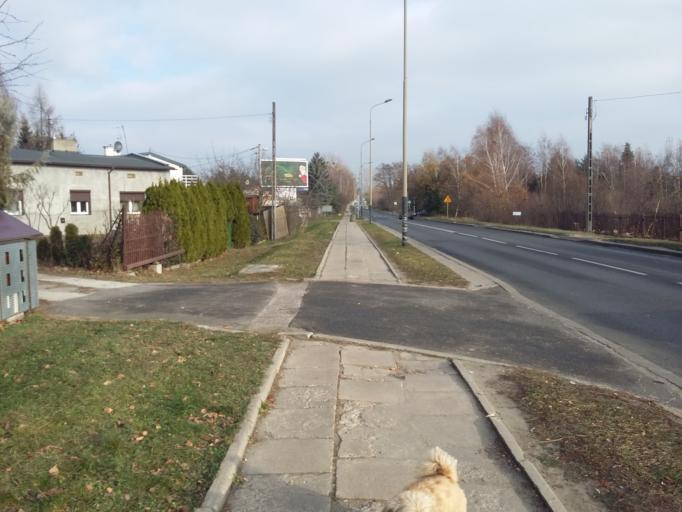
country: PL
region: Lodz Voivodeship
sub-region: Powiat pabianicki
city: Ksawerow
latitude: 51.7380
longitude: 19.4118
